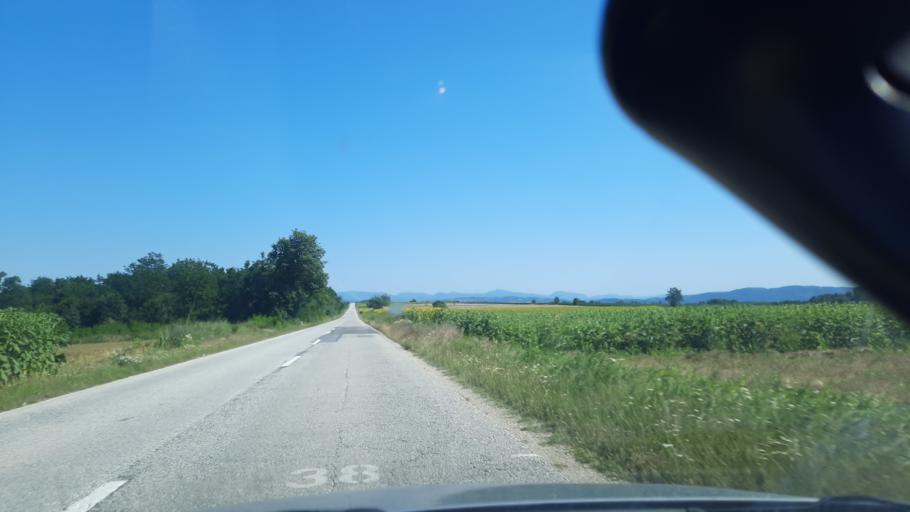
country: RS
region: Central Serbia
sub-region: Branicevski Okrug
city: Malo Crnice
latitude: 44.5729
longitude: 21.4249
